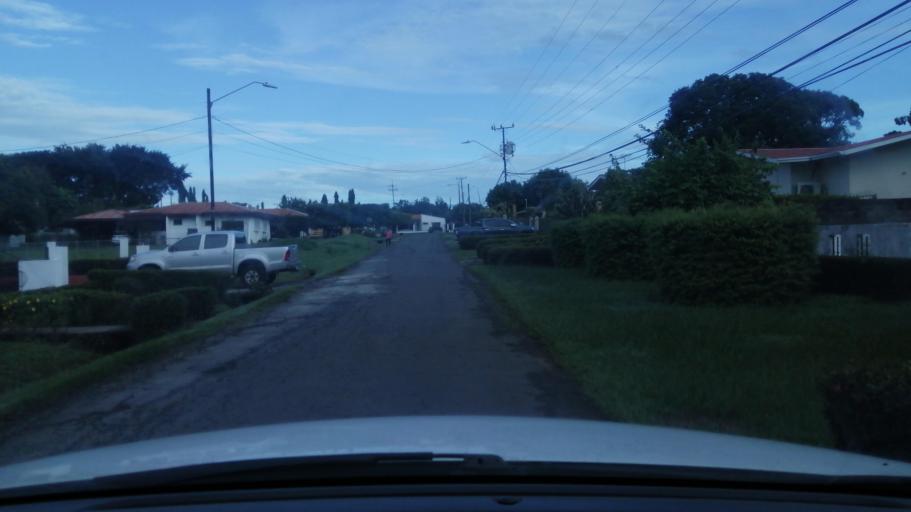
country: PA
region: Chiriqui
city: El Quiteno
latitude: 8.4585
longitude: -82.4168
